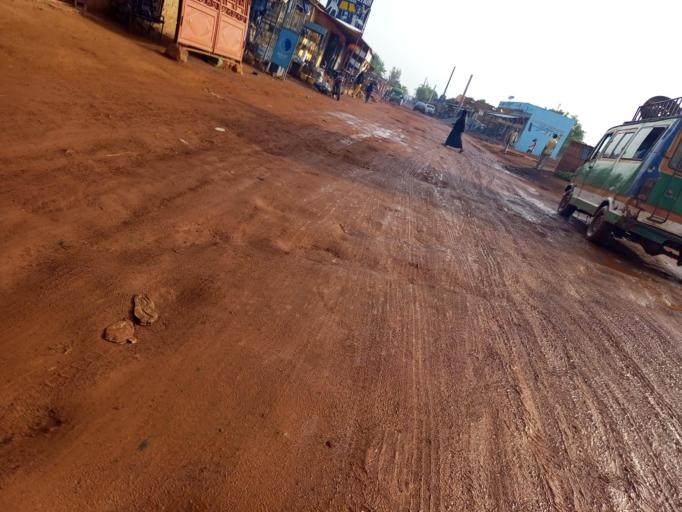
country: ML
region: Bamako
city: Bamako
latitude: 12.5243
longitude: -7.9948
